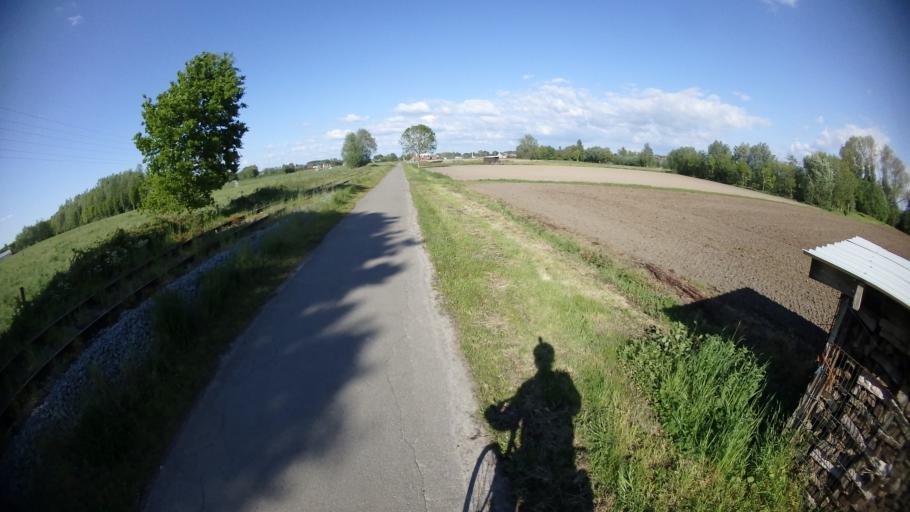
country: BE
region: Flanders
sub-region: Provincie Antwerpen
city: Sint-Amands
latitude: 51.0659
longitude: 4.2344
